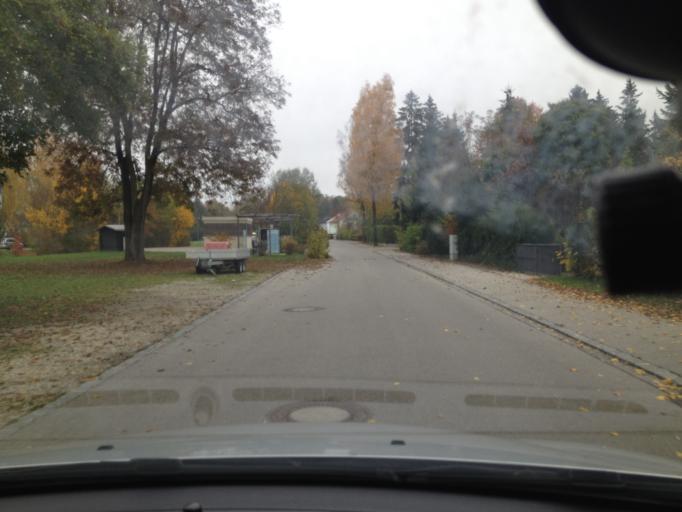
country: DE
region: Bavaria
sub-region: Swabia
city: Hiltenfingen
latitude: 48.1761
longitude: 10.7327
